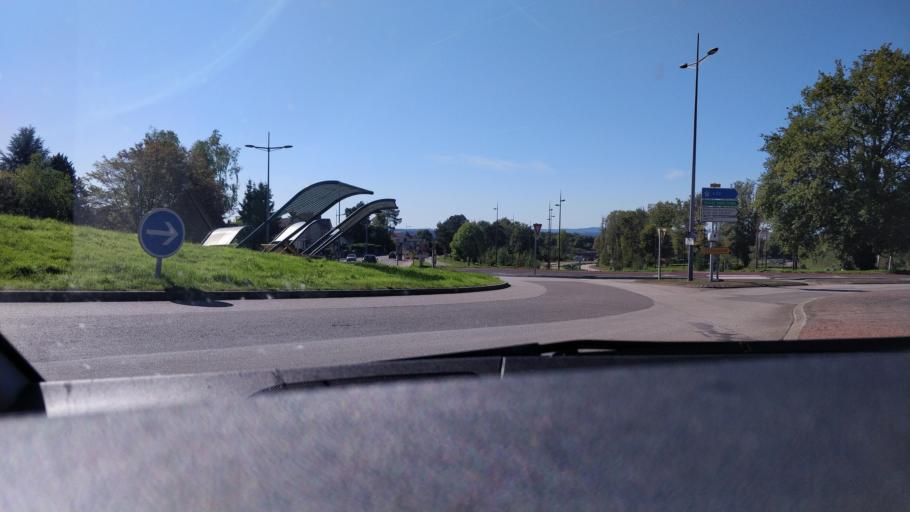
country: FR
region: Limousin
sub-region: Departement de la Haute-Vienne
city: Le Palais-sur-Vienne
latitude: 45.8604
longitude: 1.2872
